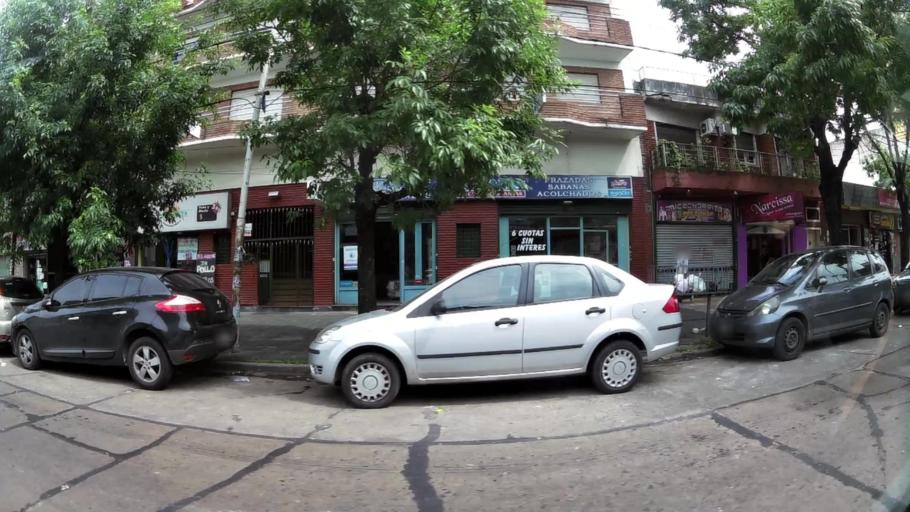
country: AR
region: Buenos Aires F.D.
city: Villa Lugano
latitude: -34.6976
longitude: -58.5064
